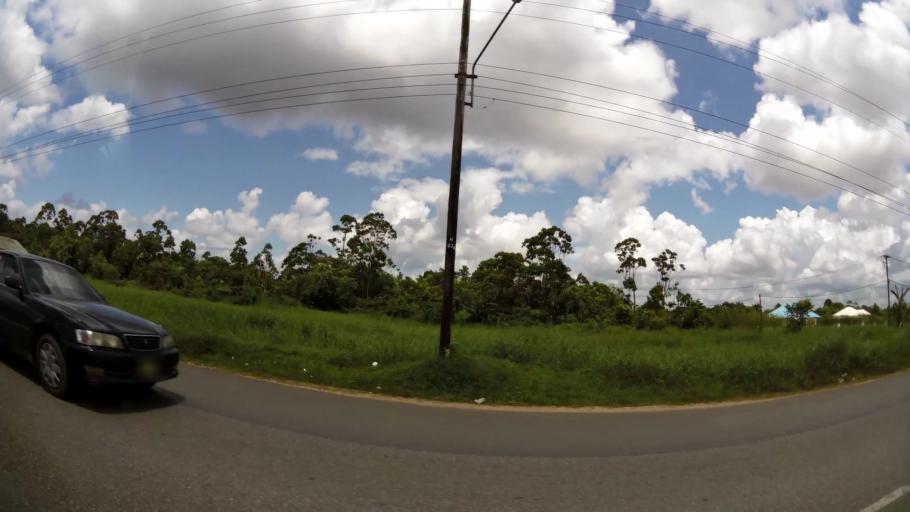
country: SR
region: Paramaribo
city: Paramaribo
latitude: 5.8040
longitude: -55.1249
